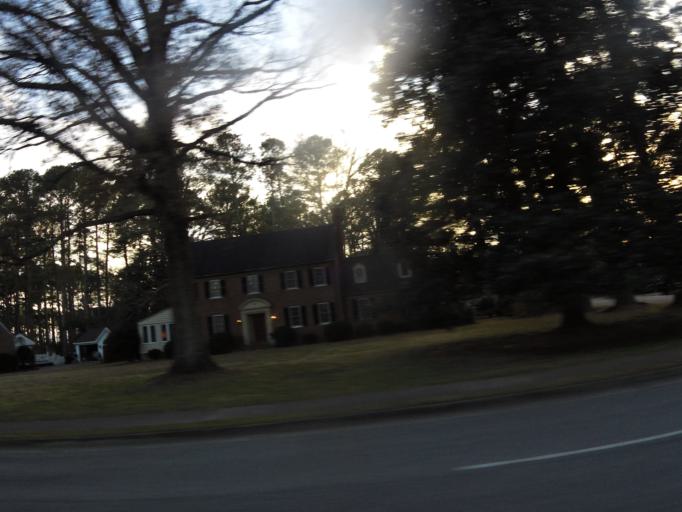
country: US
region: Virginia
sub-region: City of Franklin
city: Franklin
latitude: 36.6821
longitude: -76.9363
